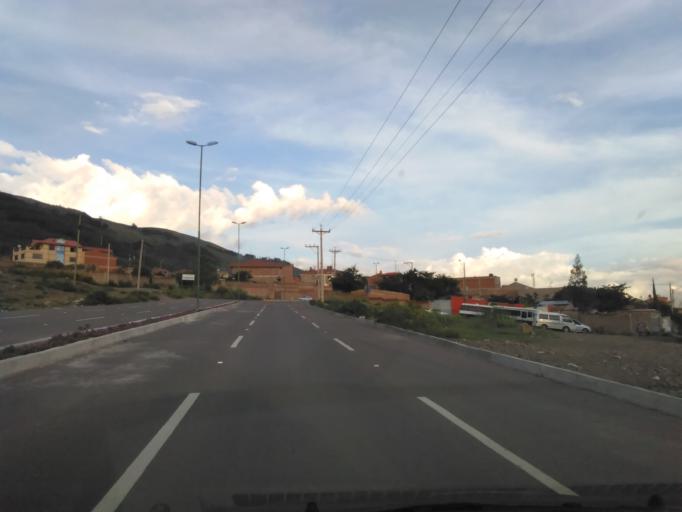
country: BO
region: Cochabamba
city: Cochabamba
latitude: -17.3507
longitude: -66.1647
